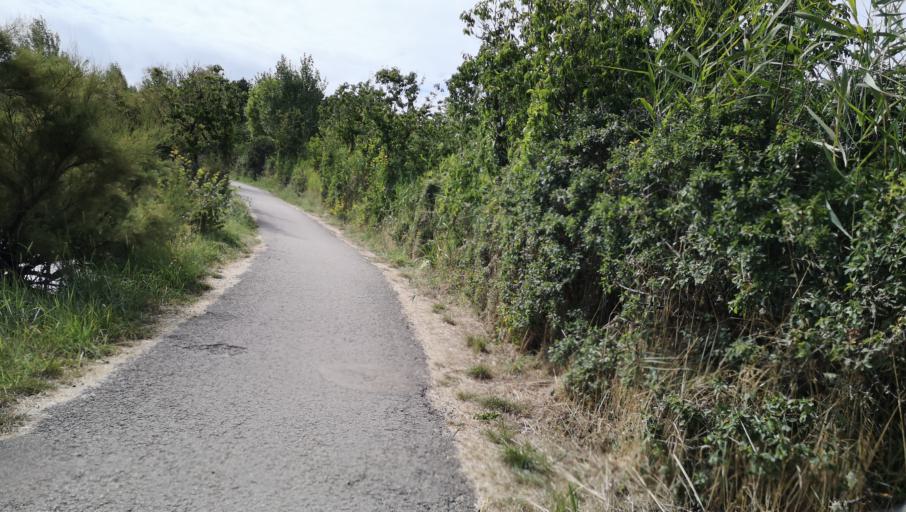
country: FR
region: Pays de la Loire
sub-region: Departement de la Vendee
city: Olonne-sur-Mer
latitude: 46.5436
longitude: -1.8059
